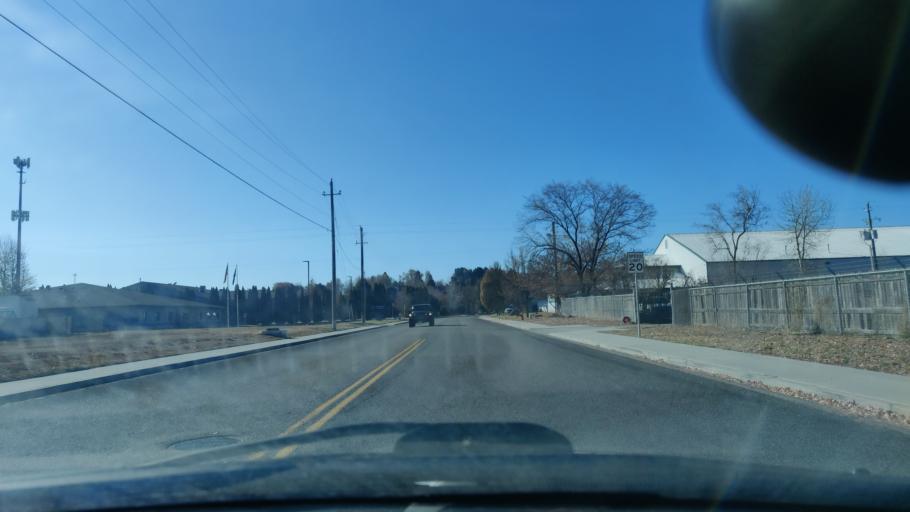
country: US
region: Idaho
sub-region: Ada County
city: Garden City
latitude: 43.6454
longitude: -116.2637
